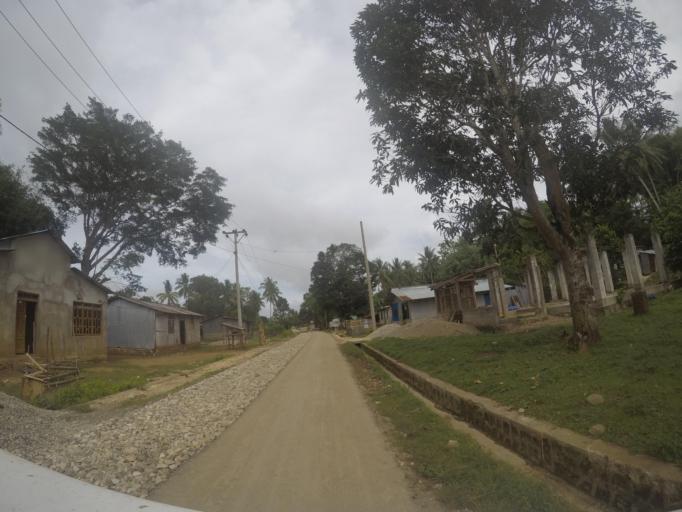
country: TL
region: Lautem
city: Lospalos
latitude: -8.5030
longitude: 126.9691
